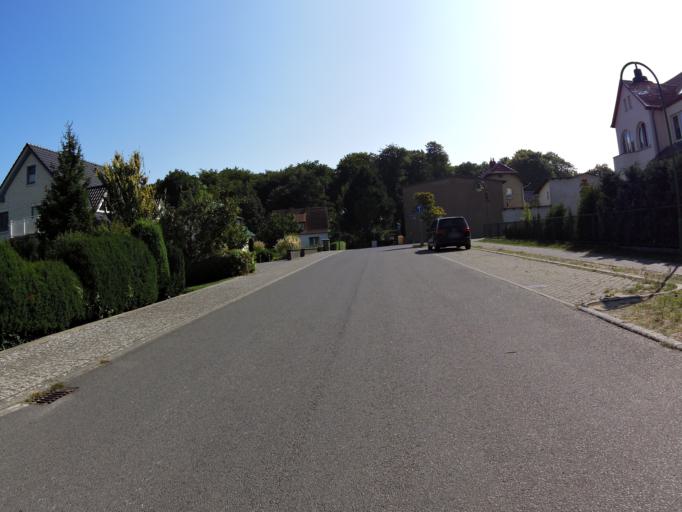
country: DE
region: Mecklenburg-Vorpommern
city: Loddin
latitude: 54.0162
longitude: 14.0522
